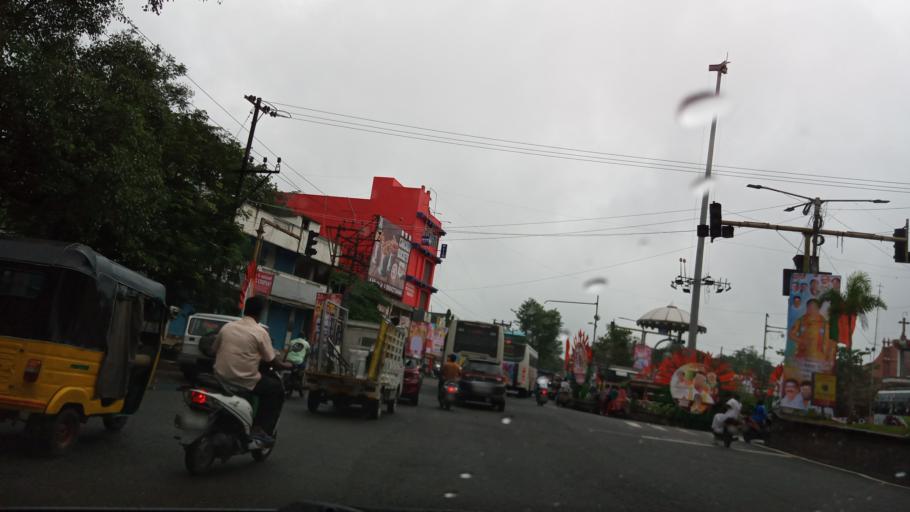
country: IN
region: Pondicherry
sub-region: Puducherry
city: Puducherry
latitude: 11.9313
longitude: 79.8194
